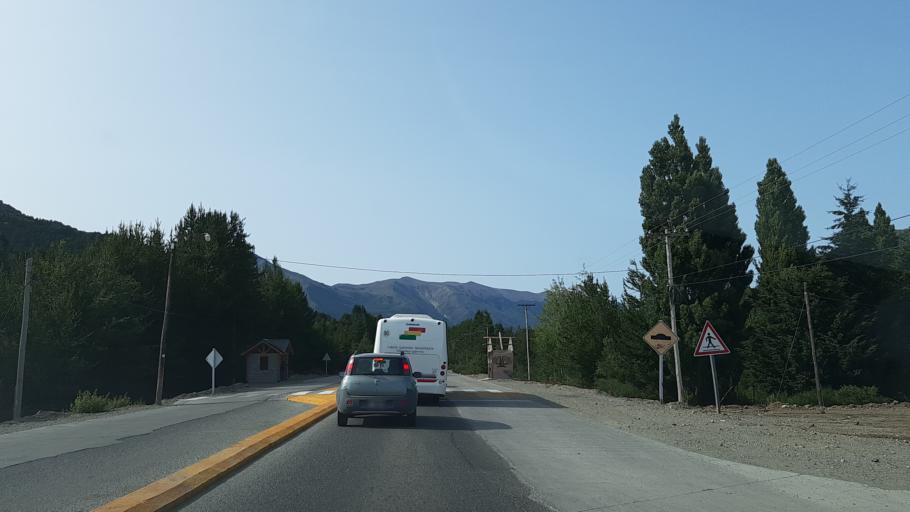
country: AR
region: Rio Negro
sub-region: Departamento de Bariloche
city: San Carlos de Bariloche
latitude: -41.1441
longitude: -71.4104
